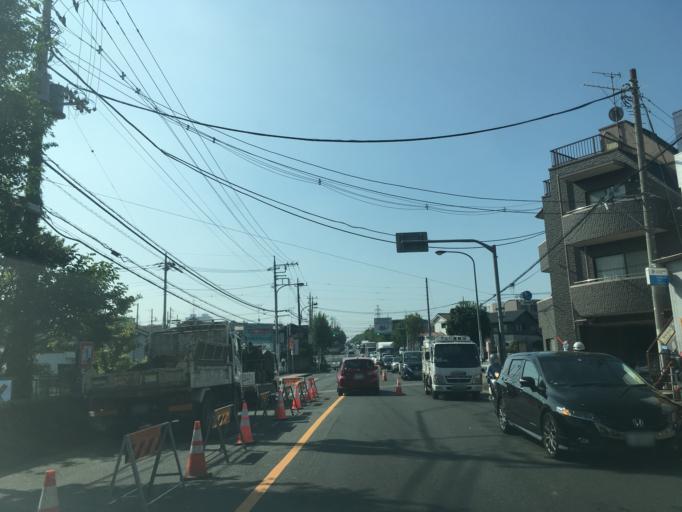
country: JP
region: Tokyo
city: Hino
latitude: 35.6805
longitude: 139.3667
